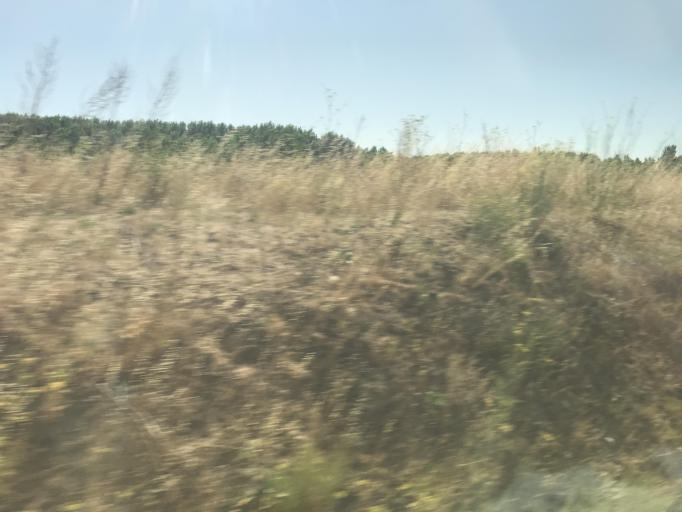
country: ES
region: Castille and Leon
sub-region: Provincia de Palencia
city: Palenzuela
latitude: 42.1109
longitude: -4.1652
